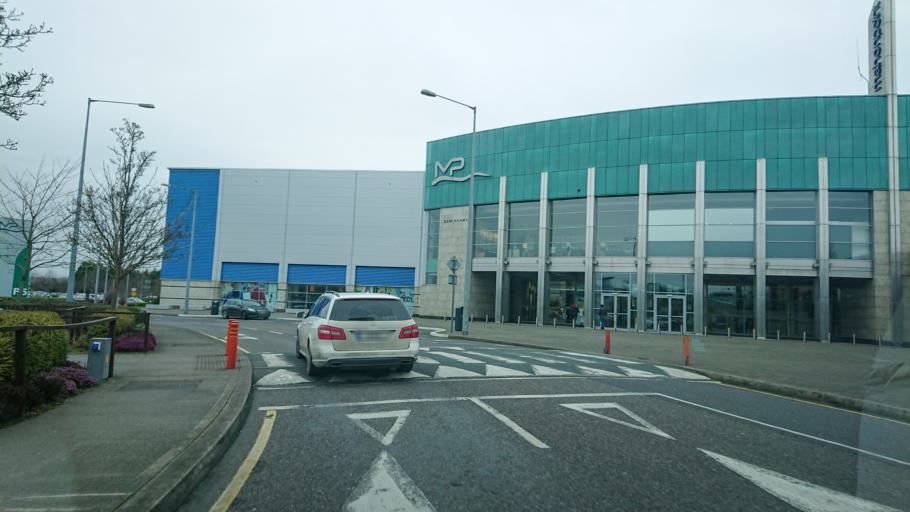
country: IE
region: Munster
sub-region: County Cork
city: Passage West
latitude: 51.8855
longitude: -8.3979
